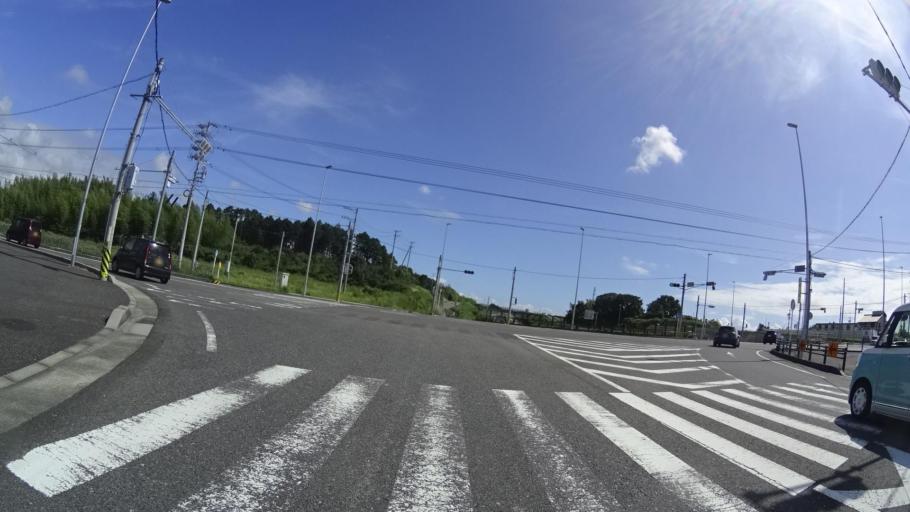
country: JP
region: Mie
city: Kawage
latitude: 34.8433
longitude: 136.5480
